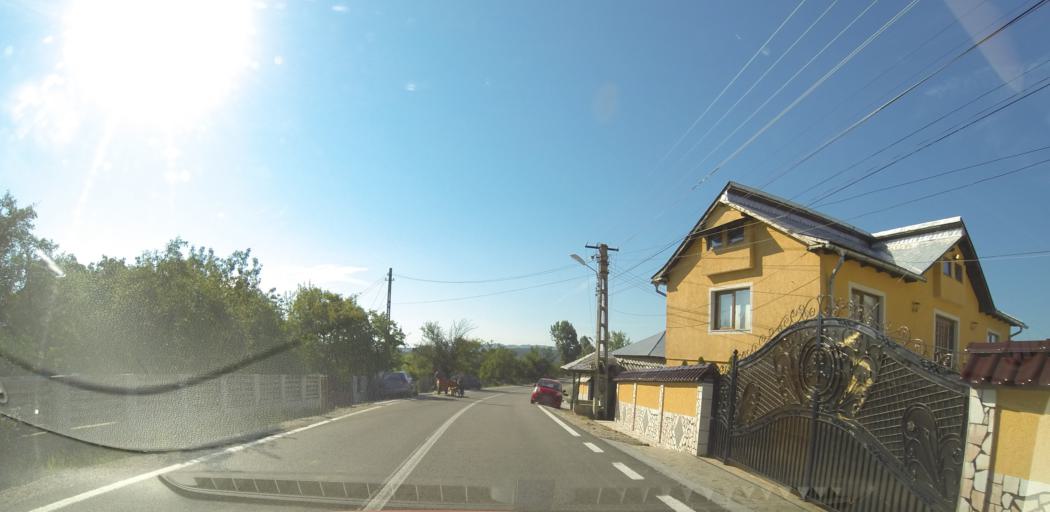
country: RO
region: Valcea
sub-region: Comuna Vaideeni
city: Vaideeni
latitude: 45.1734
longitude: 23.8734
